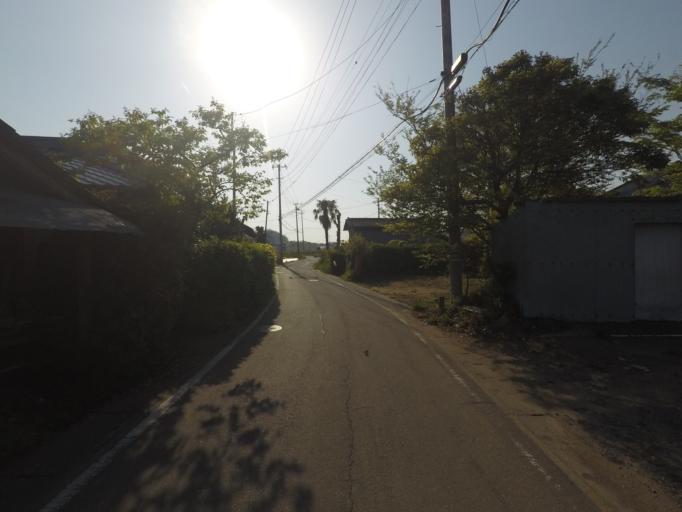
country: JP
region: Ibaraki
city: Inashiki
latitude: 36.0693
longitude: 140.3676
